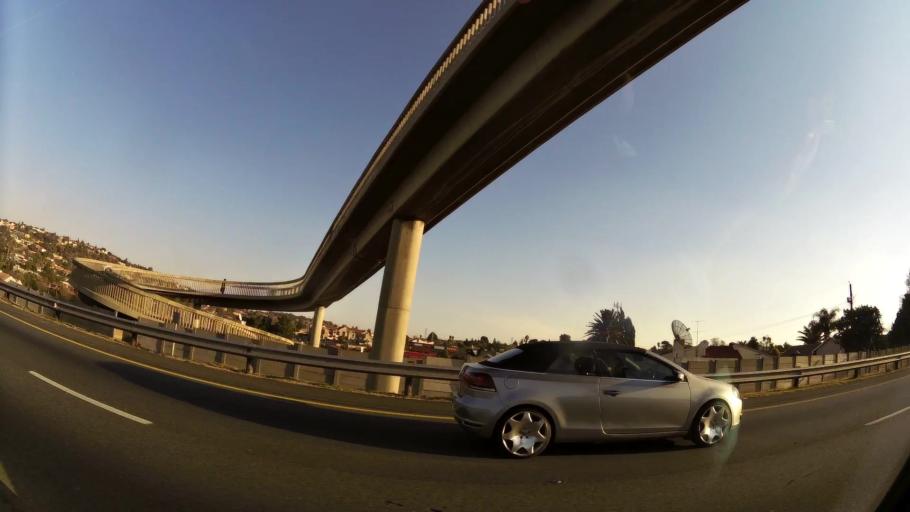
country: ZA
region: Gauteng
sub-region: City of Johannesburg Metropolitan Municipality
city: Johannesburg
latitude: -26.2703
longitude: 28.0392
